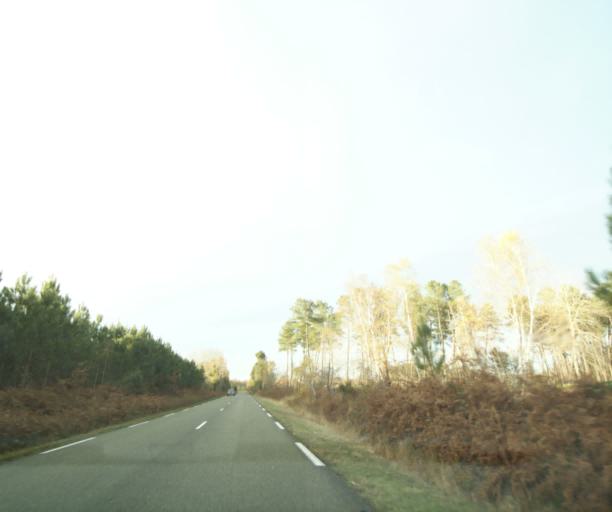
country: FR
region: Aquitaine
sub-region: Departement des Landes
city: Gabarret
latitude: 44.0931
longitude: -0.0977
